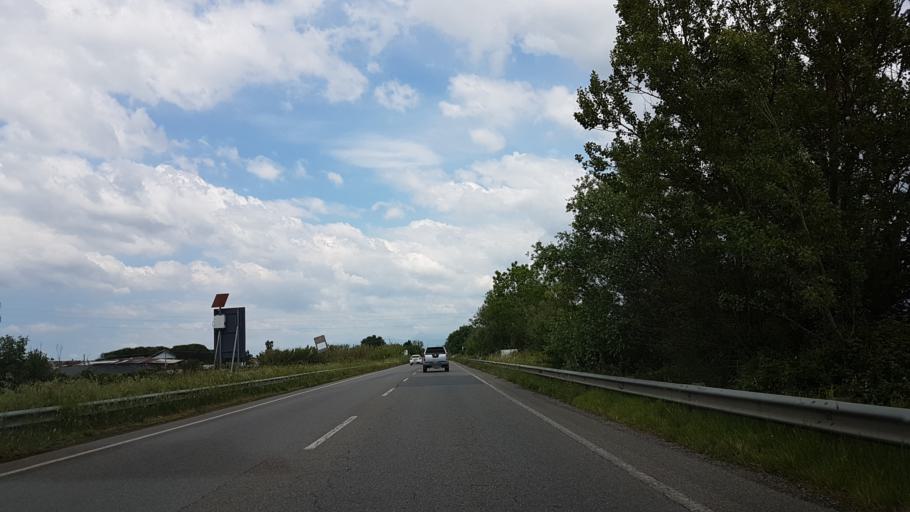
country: IT
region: Tuscany
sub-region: Provincia di Livorno
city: Vicarello
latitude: 43.6044
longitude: 10.4749
